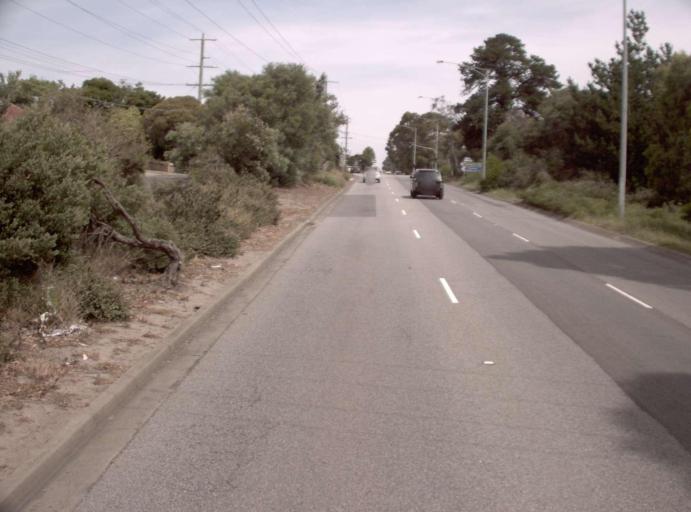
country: AU
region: Victoria
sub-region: Frankston
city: Frankston South
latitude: -38.1558
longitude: 145.1345
